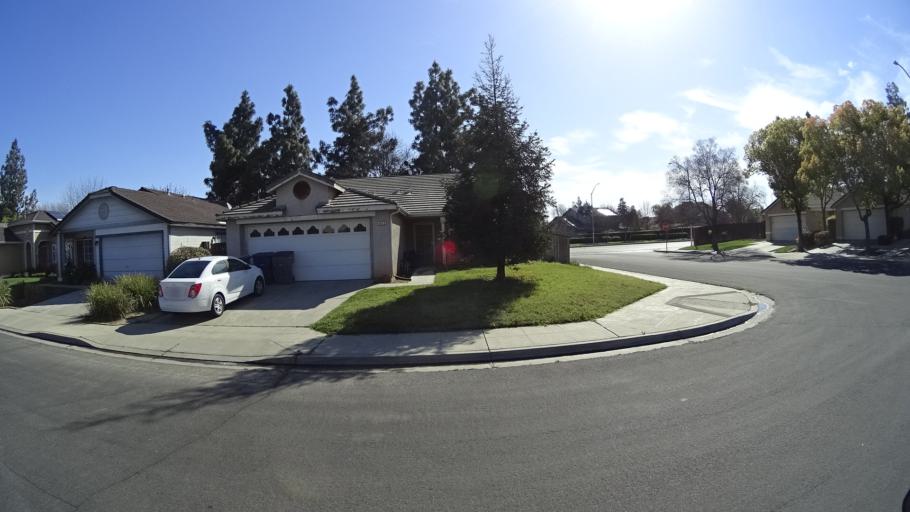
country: US
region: California
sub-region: Fresno County
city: West Park
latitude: 36.7998
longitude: -119.8901
